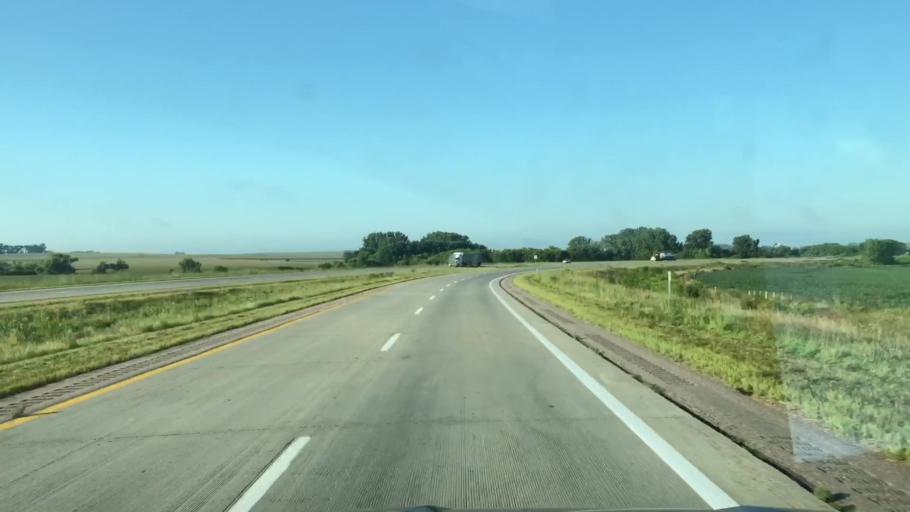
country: US
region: Iowa
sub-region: Sioux County
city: Alton
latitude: 42.9795
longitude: -95.9998
